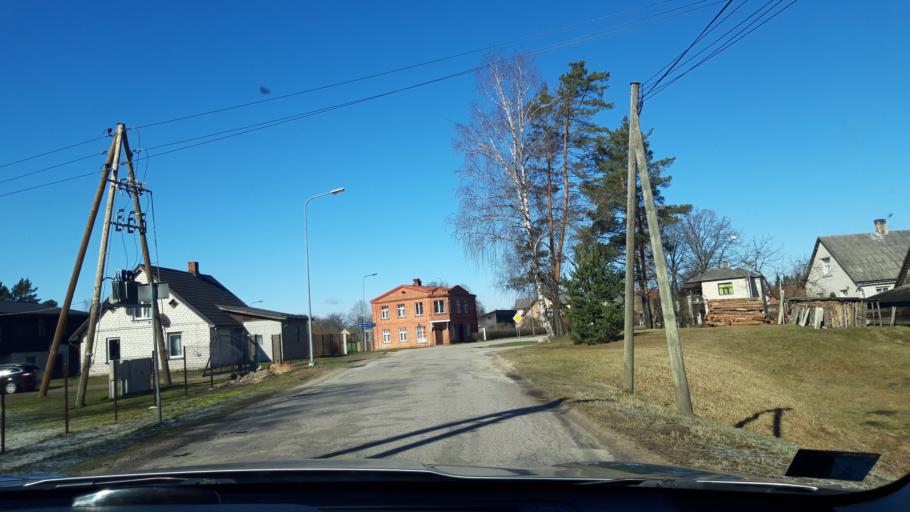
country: LV
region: Strenci
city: Strenci
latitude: 57.6234
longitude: 25.6948
